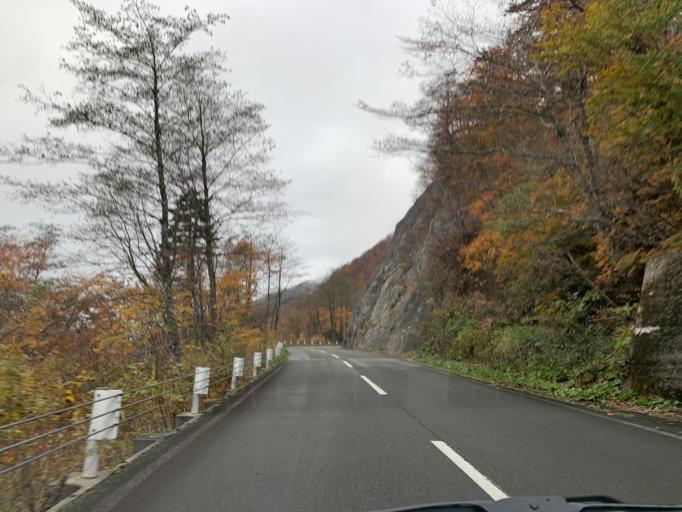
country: JP
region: Iwate
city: Mizusawa
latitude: 39.1188
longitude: 140.8328
